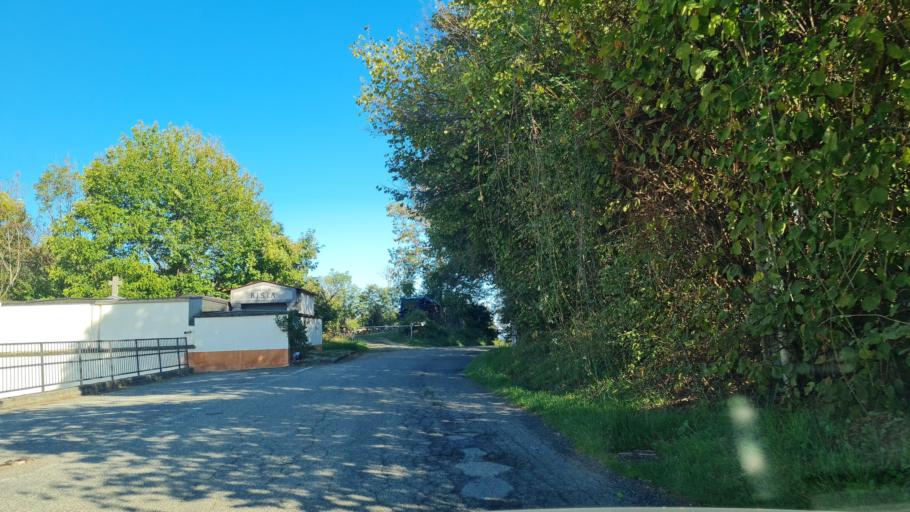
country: IT
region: Piedmont
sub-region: Provincia di Biella
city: Zubiena
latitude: 45.4910
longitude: 8.0025
